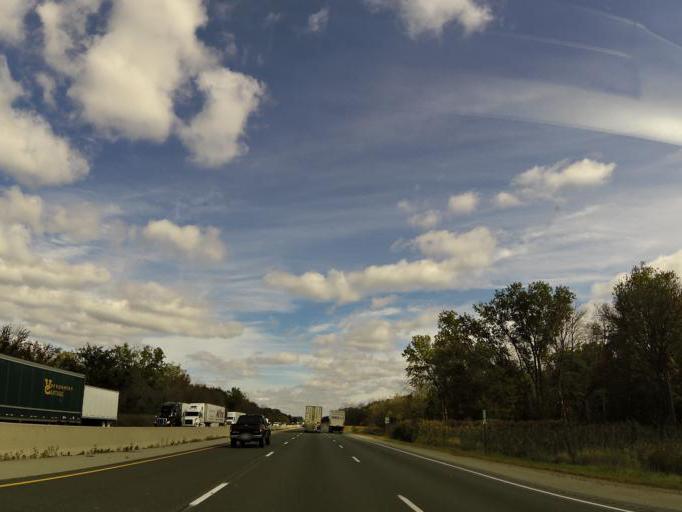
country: CA
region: Ontario
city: Dorchester
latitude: 42.9674
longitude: -81.0044
